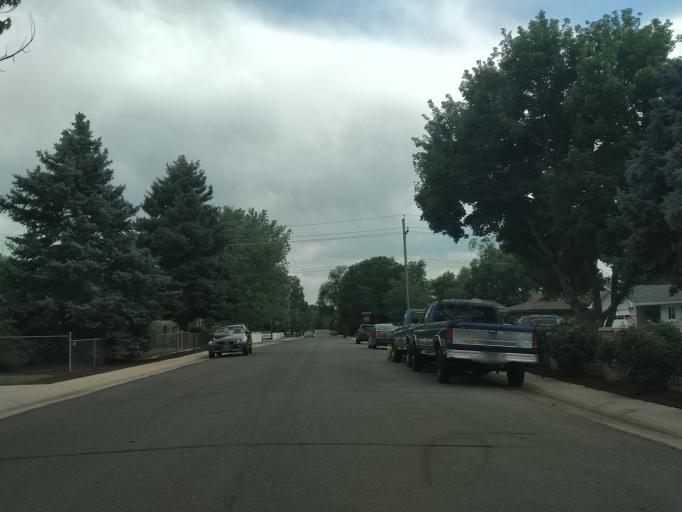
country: US
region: Colorado
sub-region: Jefferson County
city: Lakewood
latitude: 39.7011
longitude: -105.0991
